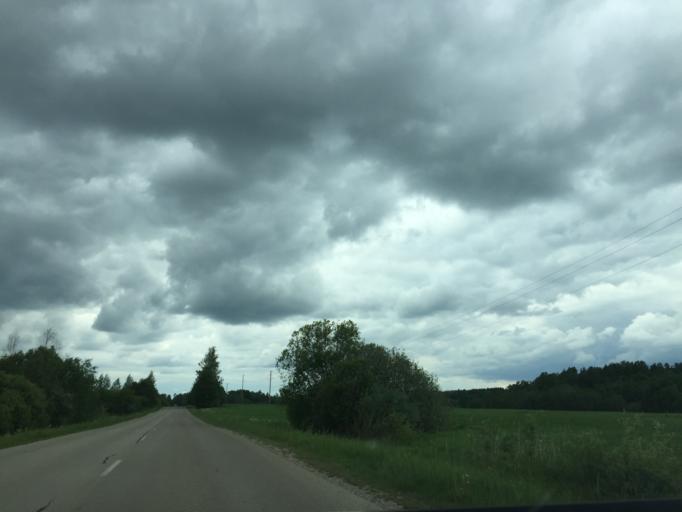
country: LV
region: Dagda
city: Dagda
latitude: 56.1101
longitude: 27.4869
